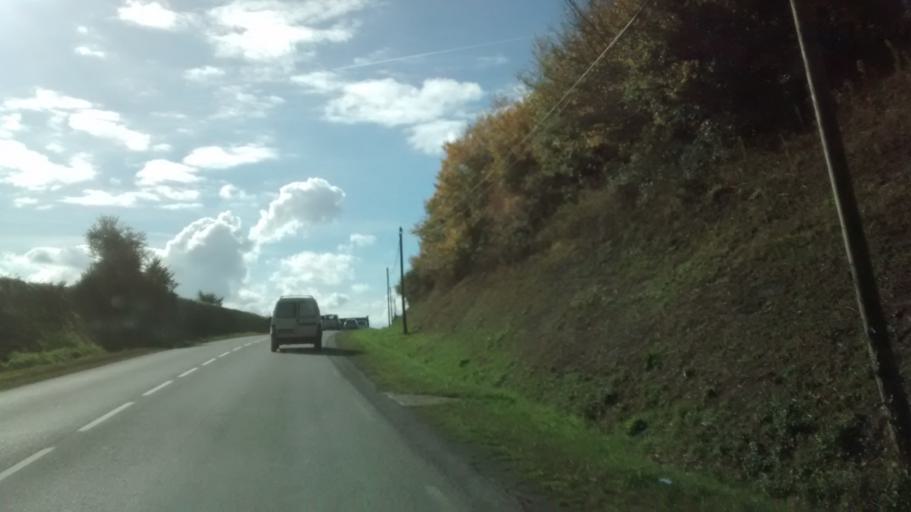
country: FR
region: Brittany
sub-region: Departement d'Ille-et-Vilaine
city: Baguer-Pican
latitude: 48.5646
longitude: -1.7041
